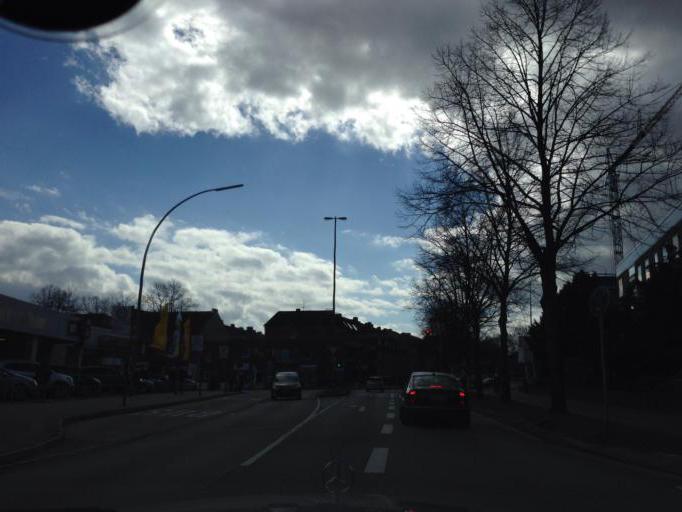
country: DE
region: Hamburg
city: Wandsbek
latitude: 53.5394
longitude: 10.1103
